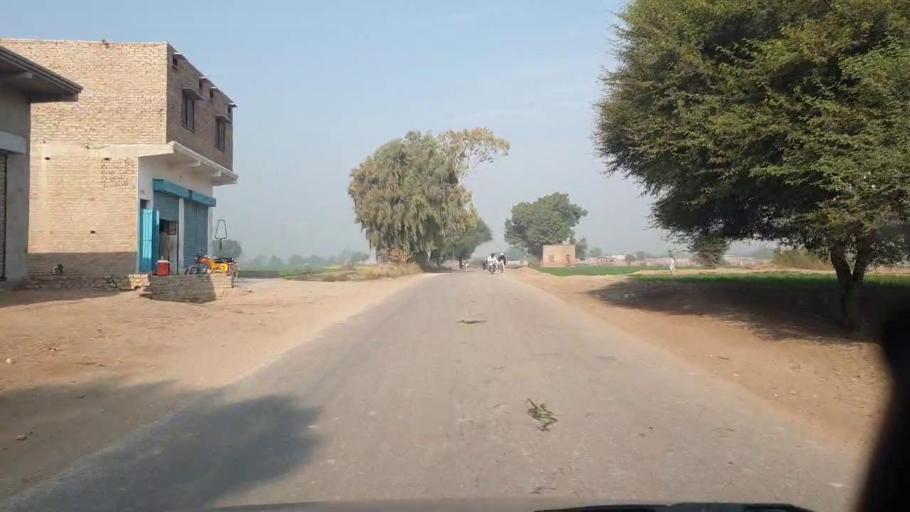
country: PK
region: Sindh
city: Shahdadpur
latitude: 25.9361
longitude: 68.6070
